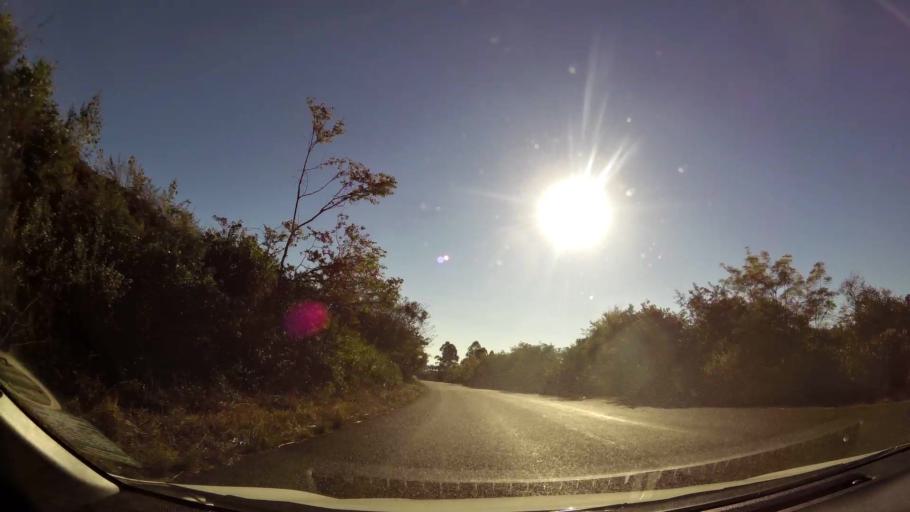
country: ZA
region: Limpopo
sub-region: Mopani District Municipality
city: Tzaneen
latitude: -23.9304
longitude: 30.0406
